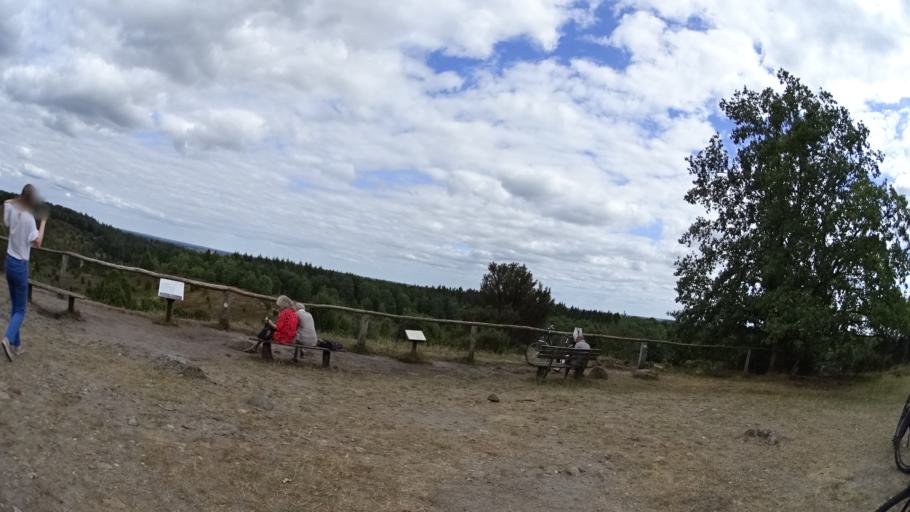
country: DE
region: Lower Saxony
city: Undeloh
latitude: 53.1549
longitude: 9.9676
